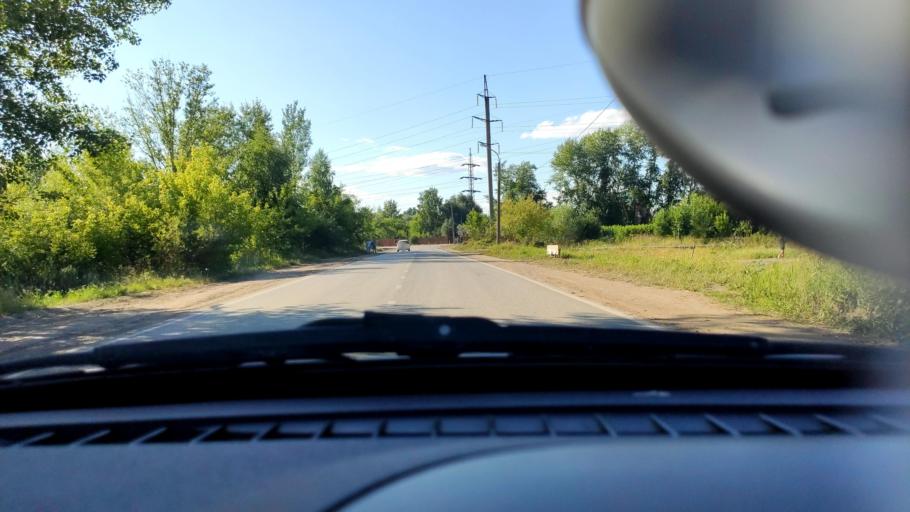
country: RU
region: Perm
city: Krasnokamsk
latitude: 58.0734
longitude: 55.7983
